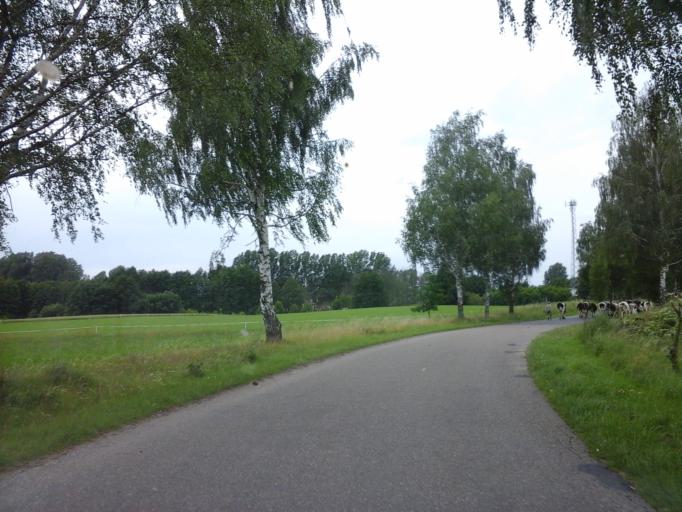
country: PL
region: West Pomeranian Voivodeship
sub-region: Powiat choszczenski
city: Bierzwnik
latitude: 53.0508
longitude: 15.6020
